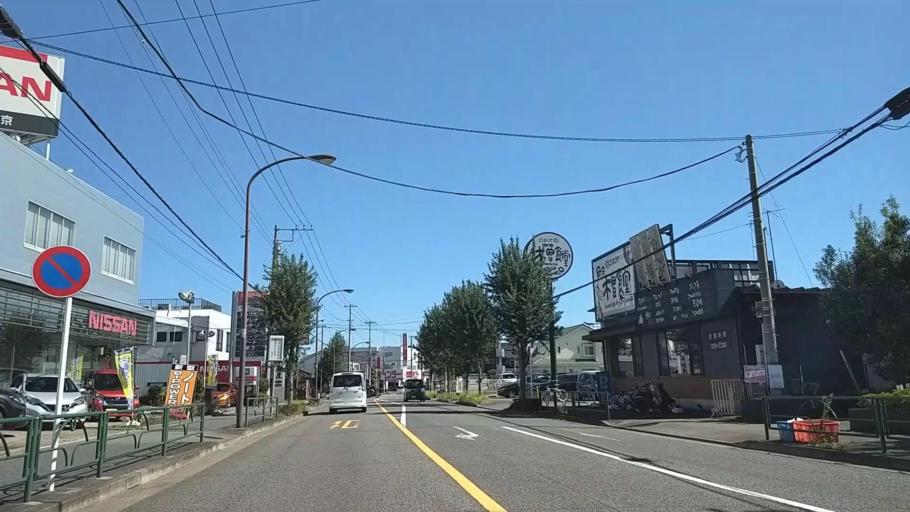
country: JP
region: Tokyo
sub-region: Machida-shi
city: Machida
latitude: 35.5750
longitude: 139.4180
